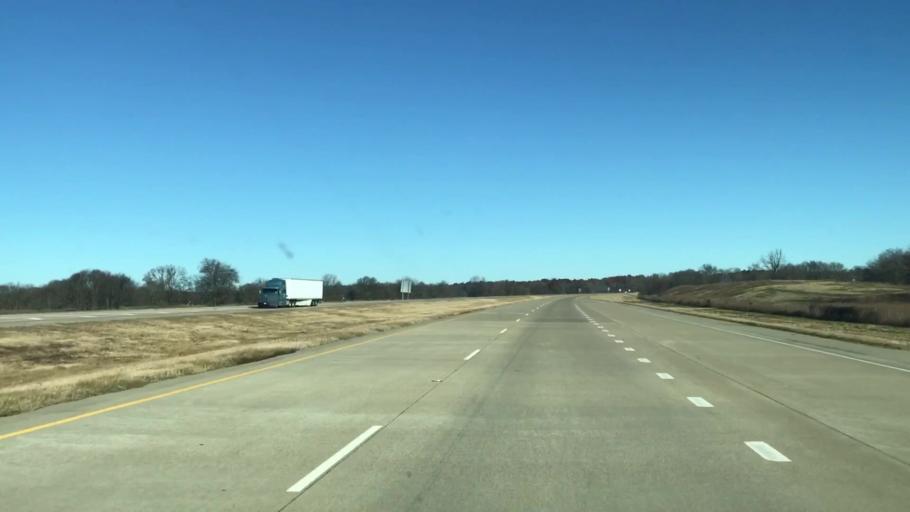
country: US
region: Louisiana
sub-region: Caddo Parish
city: Oil City
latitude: 32.7738
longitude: -93.8891
